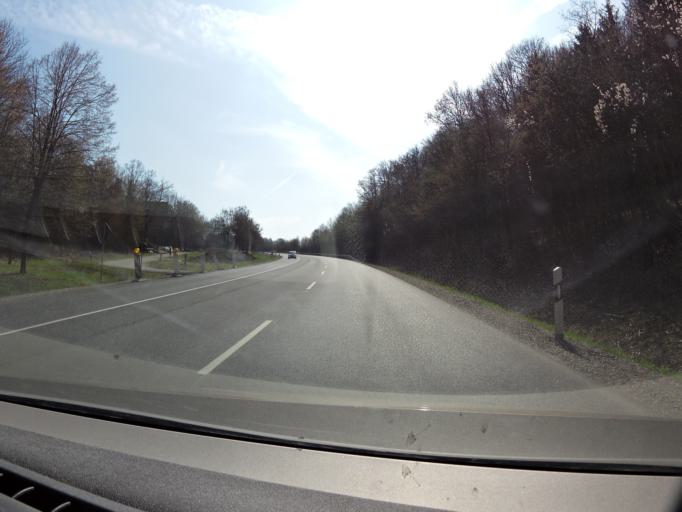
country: DE
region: Bavaria
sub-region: Regierungsbezirk Unterfranken
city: Ochsenfurt
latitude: 49.6564
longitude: 10.0725
